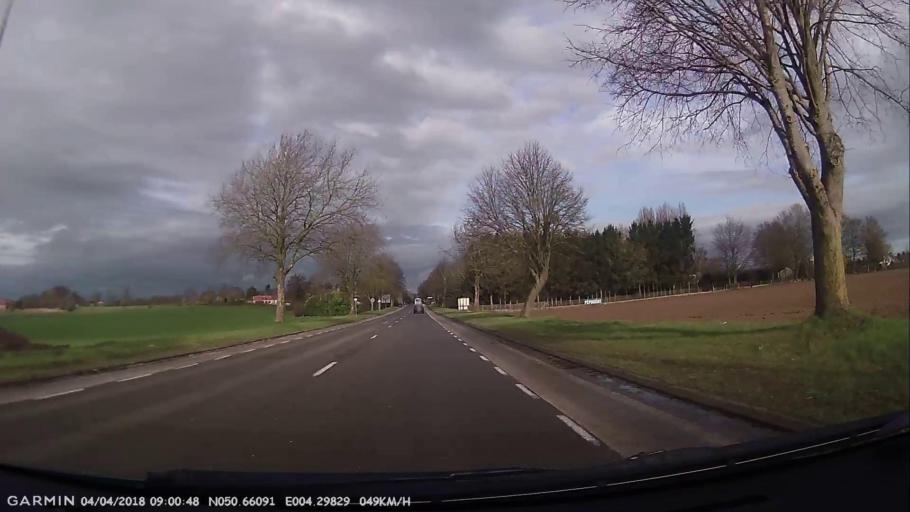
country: BE
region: Wallonia
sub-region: Province du Brabant Wallon
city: Braine-le-Chateau
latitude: 50.6610
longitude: 4.2980
